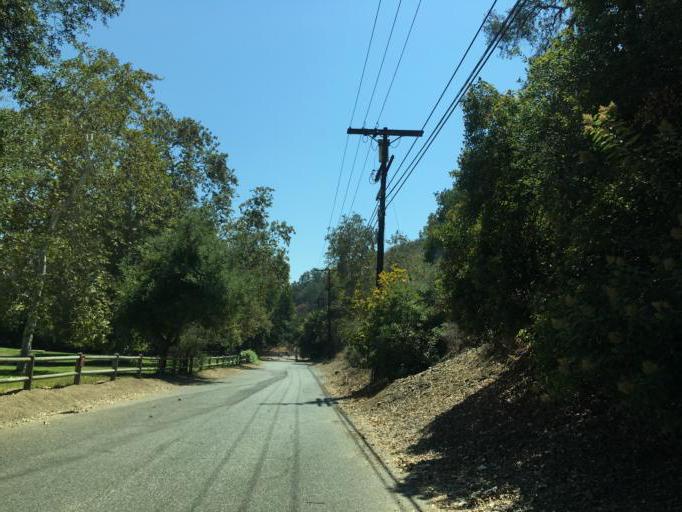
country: US
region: California
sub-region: Los Angeles County
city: Beverly Hills
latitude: 34.1063
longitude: -118.4152
